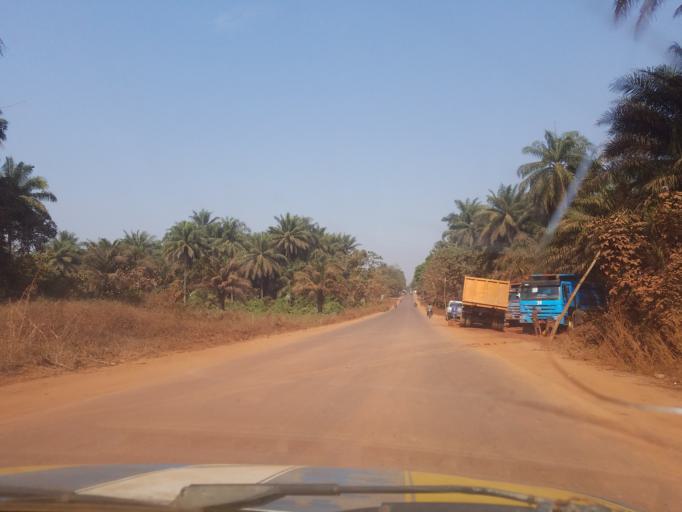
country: GN
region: Boke
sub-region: Boke Prefecture
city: Sangueya
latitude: 10.8020
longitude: -14.3917
